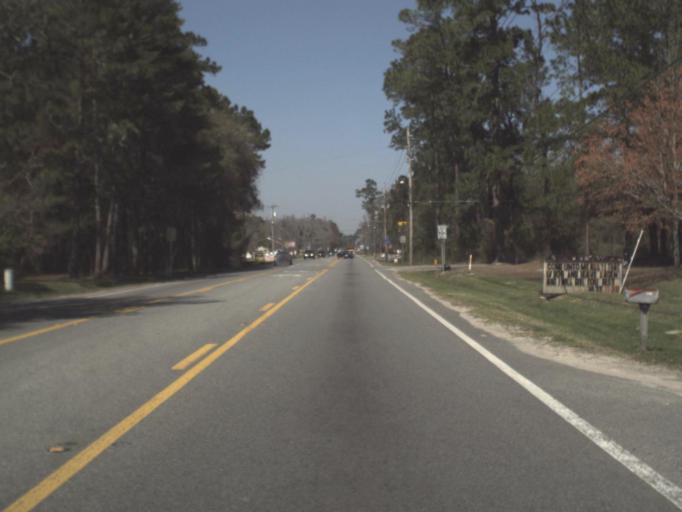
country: US
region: Florida
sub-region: Leon County
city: Woodville
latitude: 30.3186
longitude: -84.2484
